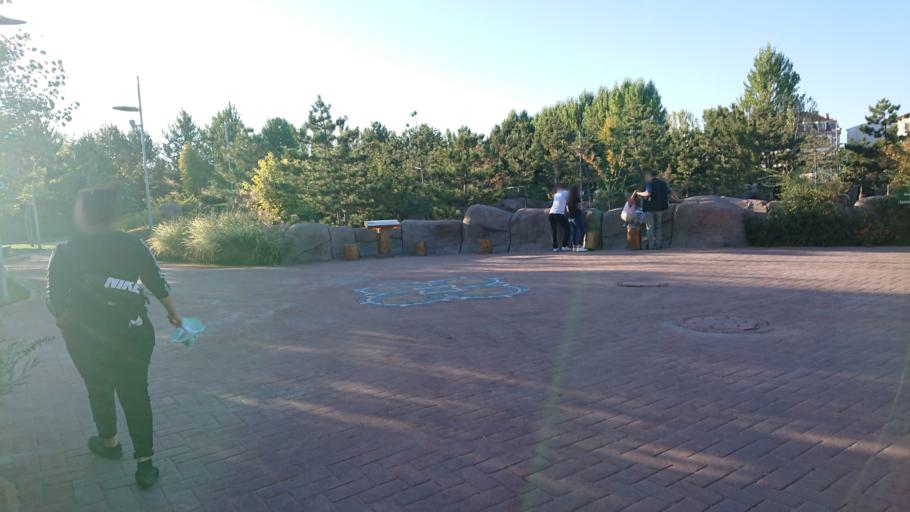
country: TR
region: Eskisehir
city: Eskisehir
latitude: 39.7696
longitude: 30.4747
